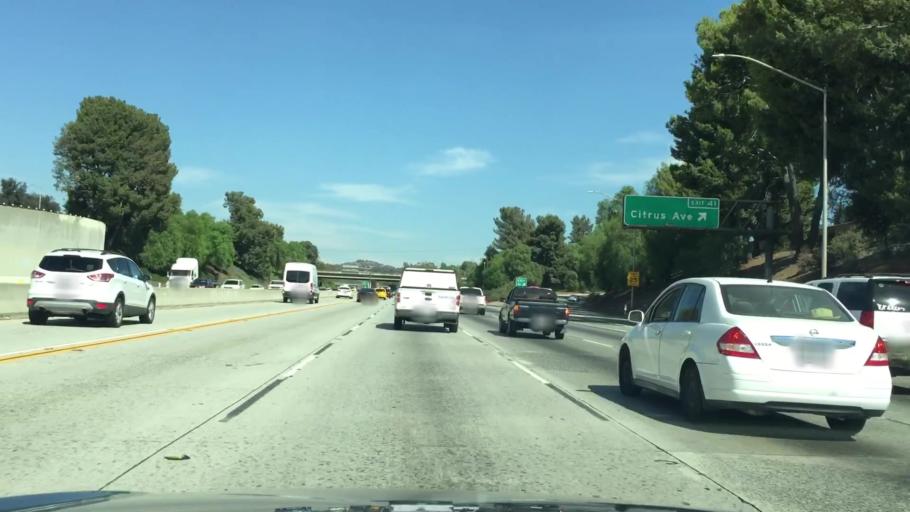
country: US
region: California
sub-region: Los Angeles County
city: Citrus
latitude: 34.1207
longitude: -117.8941
